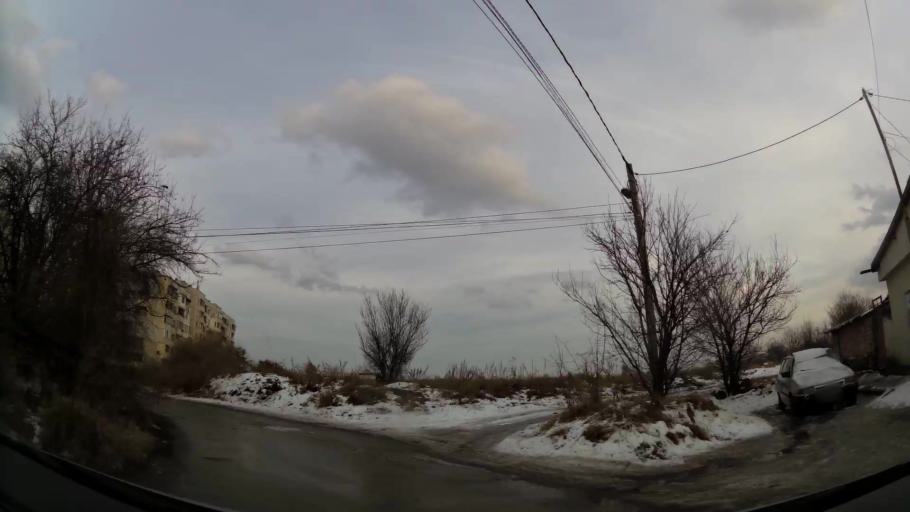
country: BG
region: Sofia-Capital
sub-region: Stolichna Obshtina
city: Sofia
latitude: 42.7211
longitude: 23.3477
